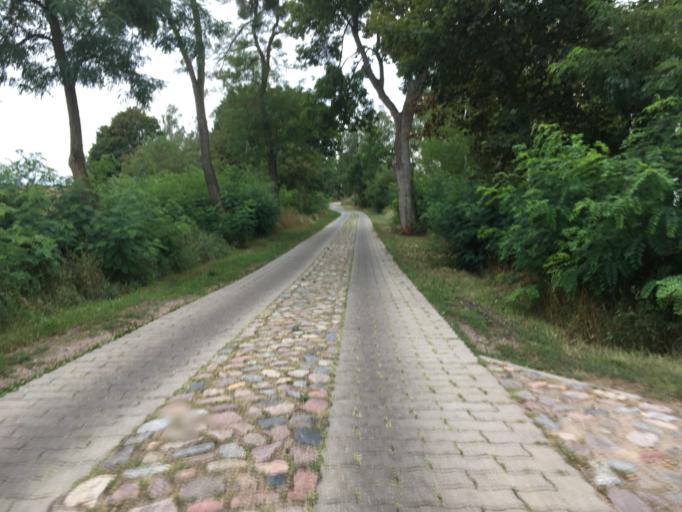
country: DE
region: Brandenburg
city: Passow
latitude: 53.1090
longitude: 14.1219
